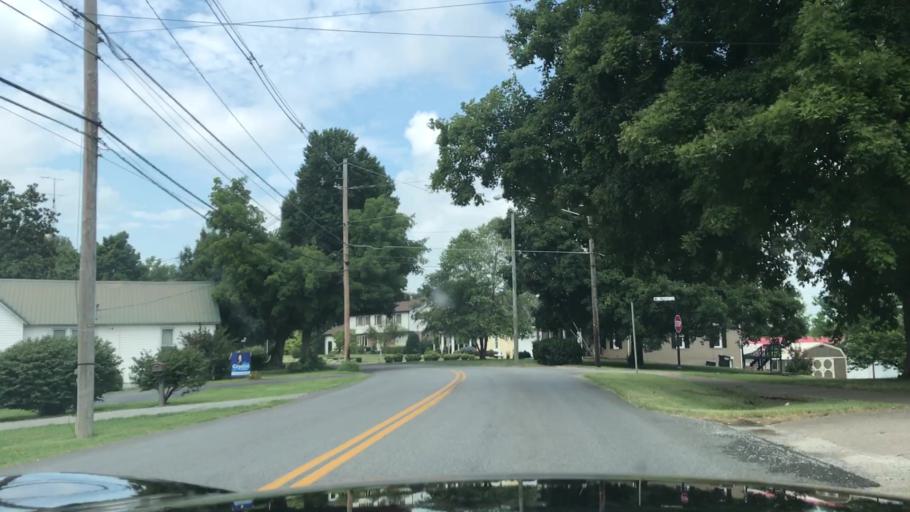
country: US
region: Kentucky
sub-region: Muhlenberg County
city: Greenville
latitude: 37.2052
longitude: -87.1694
